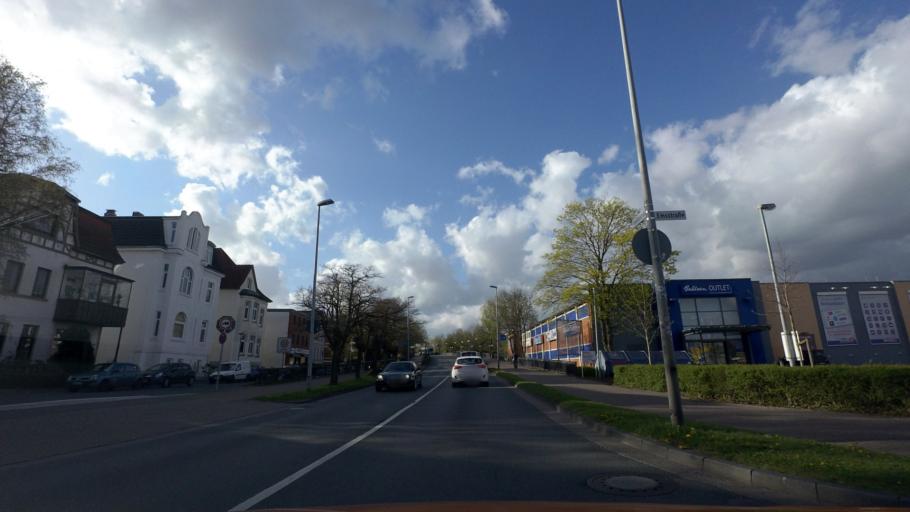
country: DE
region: Lower Saxony
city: Oldenburg
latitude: 53.1369
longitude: 8.2269
